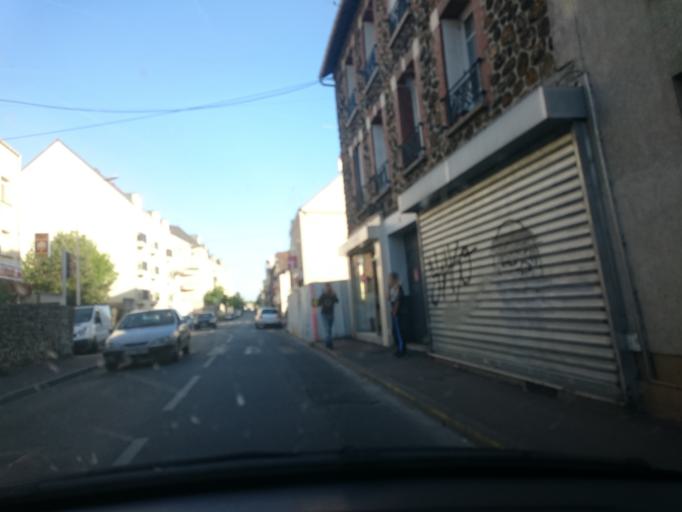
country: FR
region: Ile-de-France
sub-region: Departement de l'Essonne
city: Juvisy-sur-Orge
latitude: 48.6864
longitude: 2.3785
